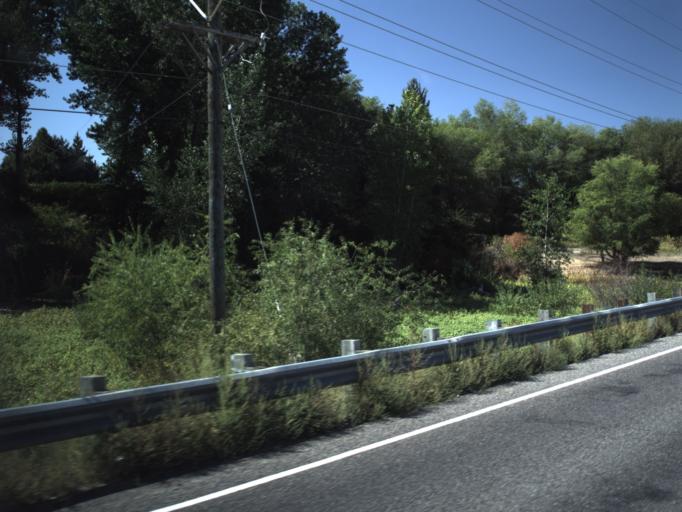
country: US
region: Utah
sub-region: Cache County
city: Smithfield
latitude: 41.8413
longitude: -111.8821
